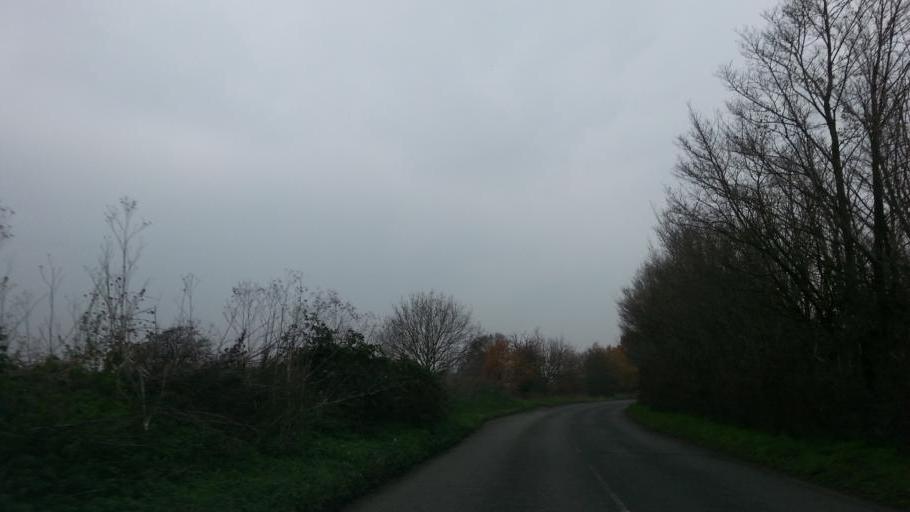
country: GB
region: England
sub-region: Suffolk
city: Thurston
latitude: 52.2316
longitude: 0.8099
